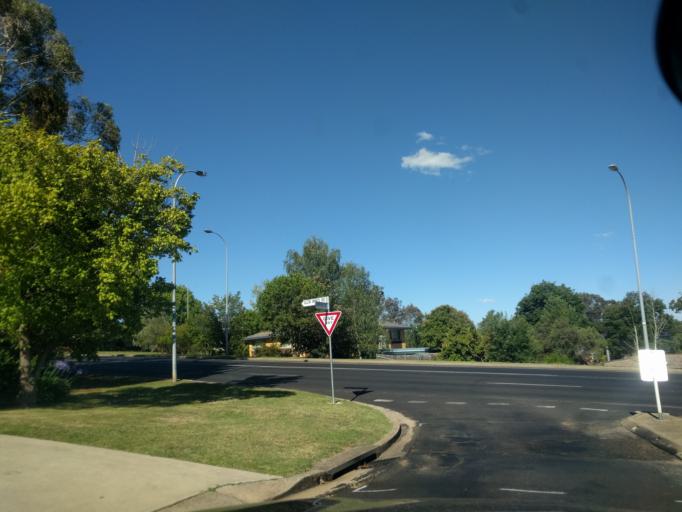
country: AU
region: New South Wales
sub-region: Armidale Dumaresq
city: Armidale
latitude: -30.4996
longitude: 151.6705
